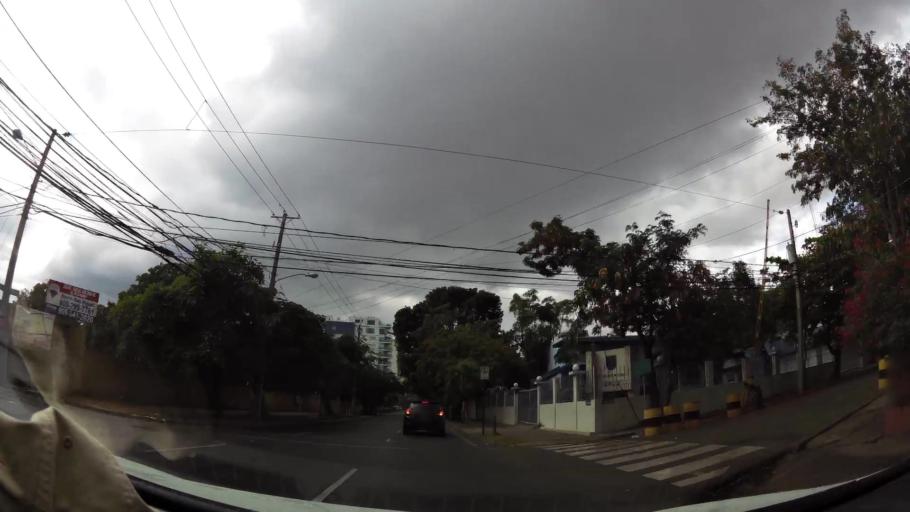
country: DO
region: Nacional
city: Ciudad Nueva
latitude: 18.4668
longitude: -69.9130
